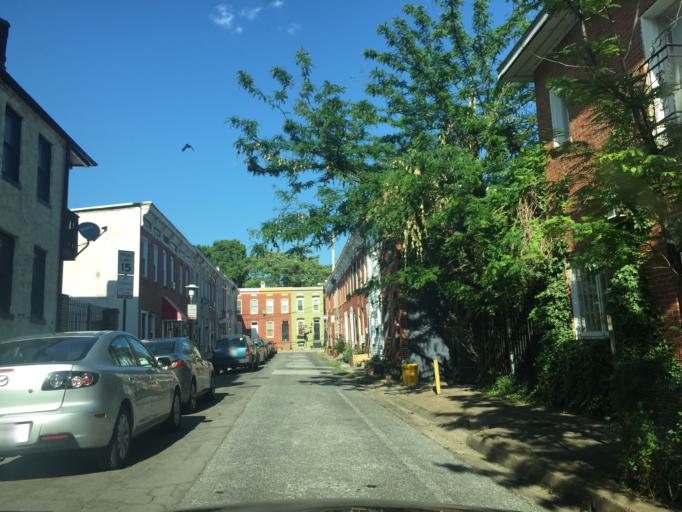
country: US
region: Maryland
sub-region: City of Baltimore
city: Baltimore
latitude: 39.2924
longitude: -76.5873
